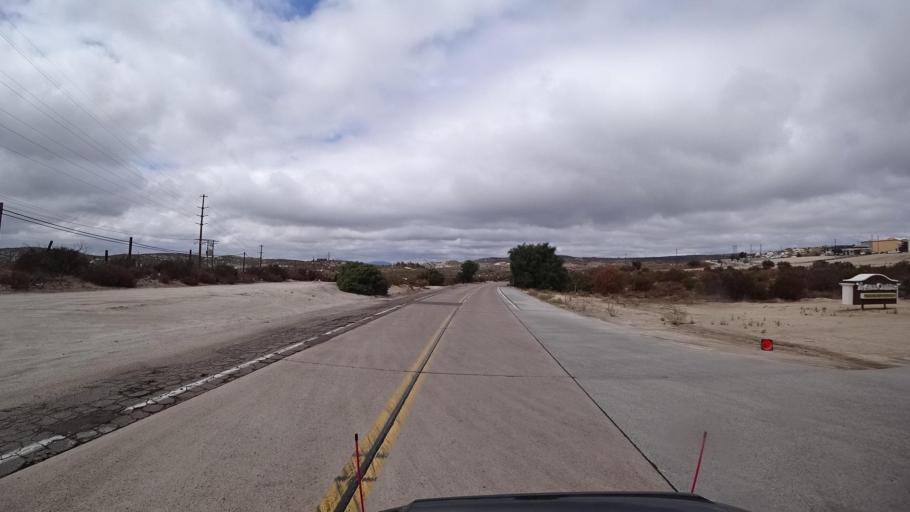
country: US
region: California
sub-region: San Diego County
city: Campo
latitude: 32.6989
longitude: -116.3546
